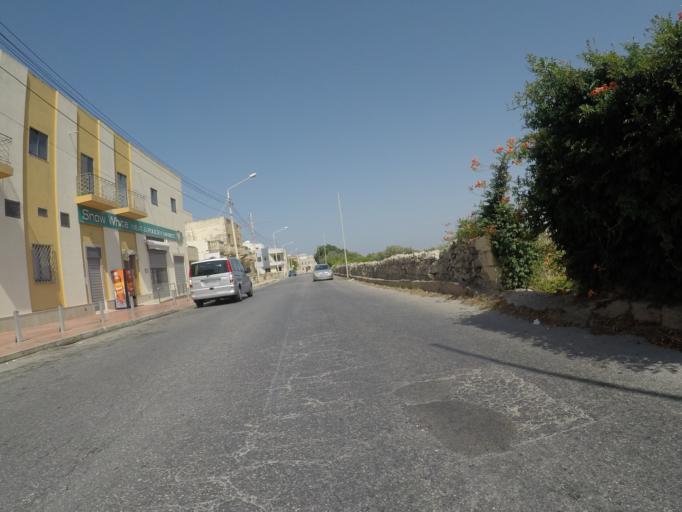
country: MT
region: L-Imgarr
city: Imgarr
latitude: 35.9187
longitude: 14.3787
